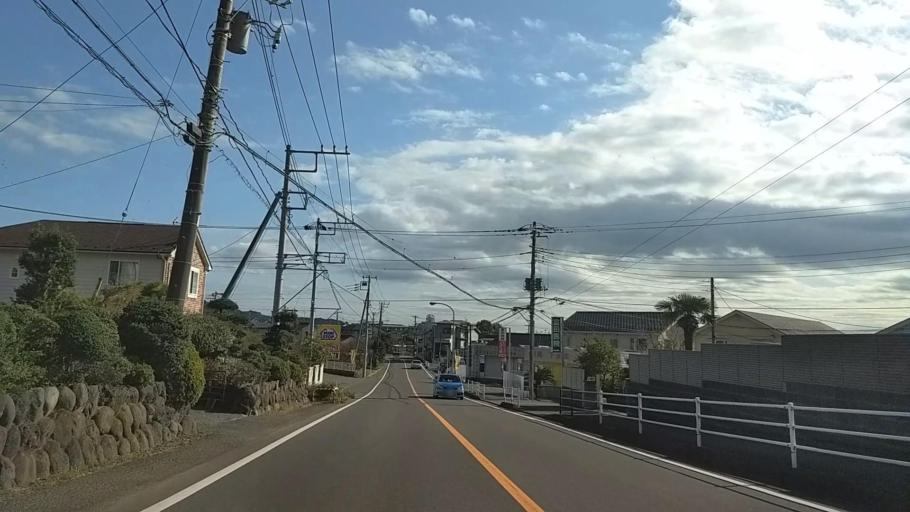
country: JP
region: Kanagawa
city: Odawara
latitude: 35.3036
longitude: 139.1877
